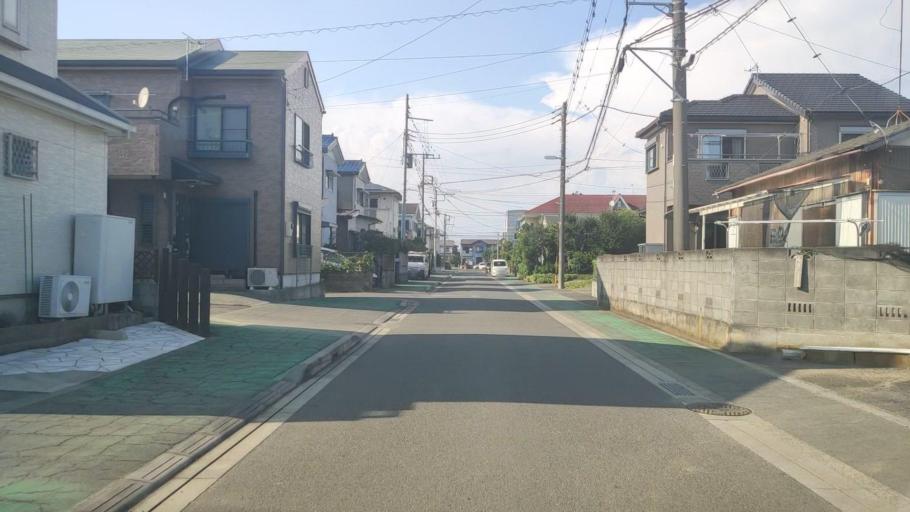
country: JP
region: Kanagawa
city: Hiratsuka
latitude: 35.3483
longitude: 139.3225
